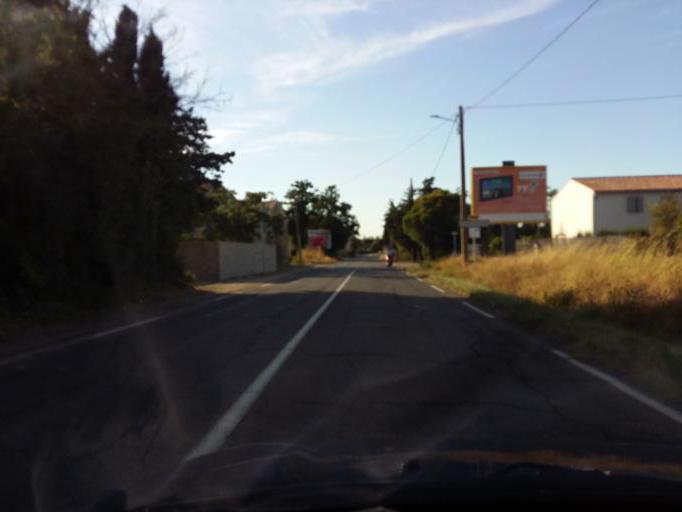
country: FR
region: Provence-Alpes-Cote d'Azur
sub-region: Departement du Vaucluse
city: Carpentras
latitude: 44.0442
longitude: 5.0610
